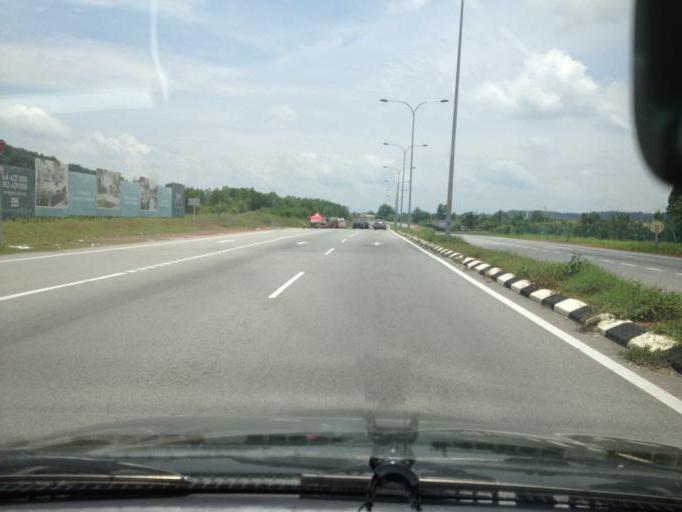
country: MY
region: Kedah
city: Sungai Petani
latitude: 5.6203
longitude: 100.5410
